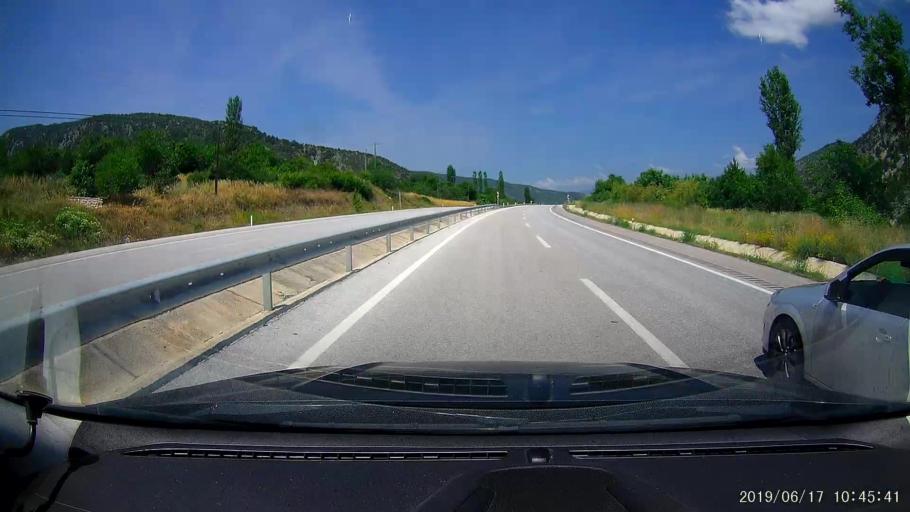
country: TR
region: Corum
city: Hacihamza
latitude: 41.0626
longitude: 34.4815
